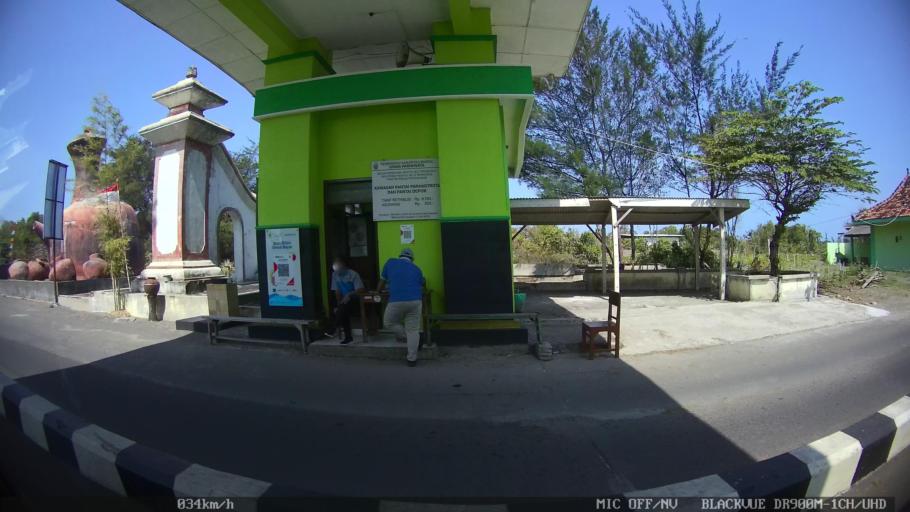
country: ID
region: Daerah Istimewa Yogyakarta
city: Bambanglipuro
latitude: -8.0099
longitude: 110.2955
